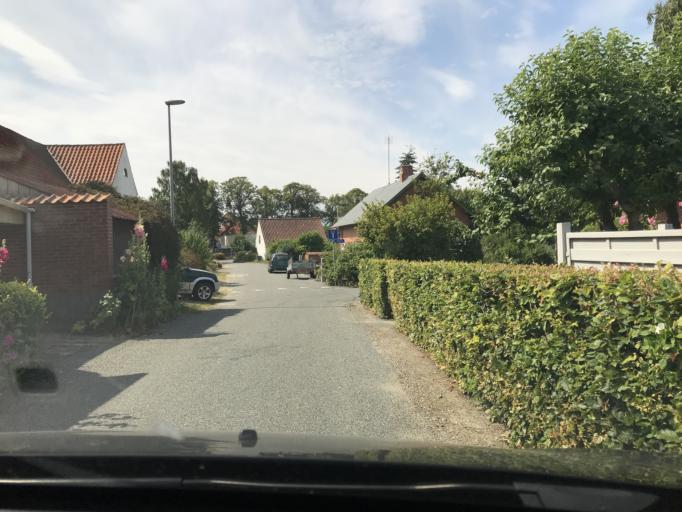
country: DK
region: South Denmark
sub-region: Faaborg-Midtfyn Kommune
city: Faaborg
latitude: 54.9380
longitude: 10.2596
